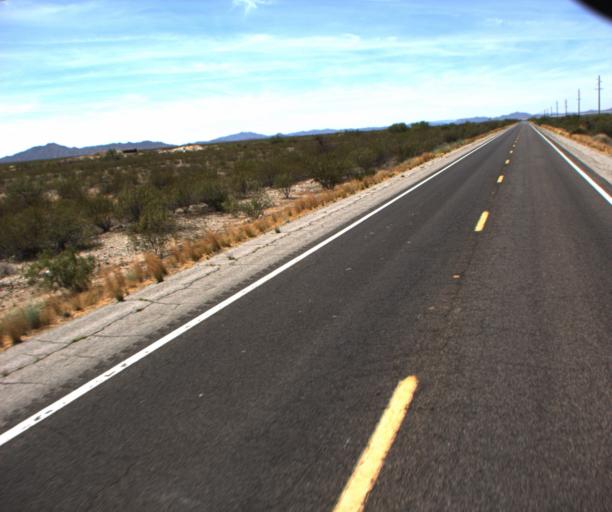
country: US
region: Arizona
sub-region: La Paz County
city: Salome
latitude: 33.8485
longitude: -113.4558
